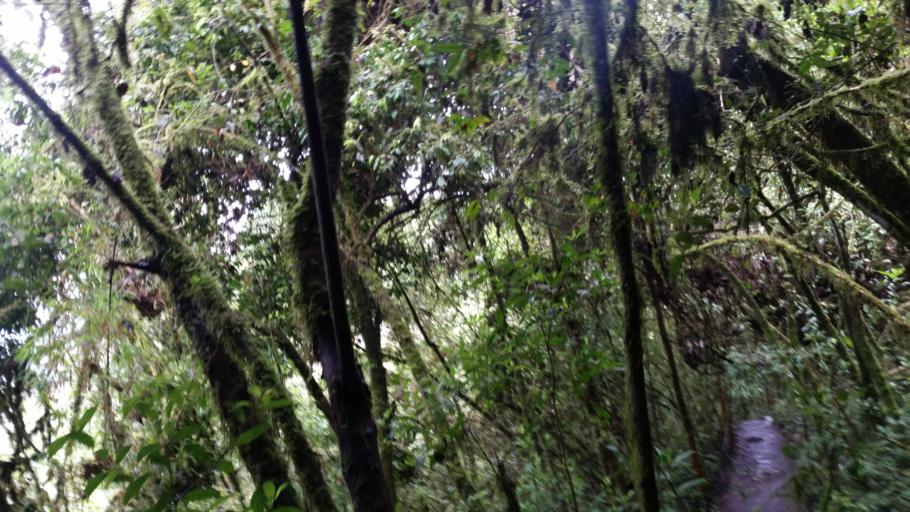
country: CO
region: Cundinamarca
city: Choachi
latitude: 4.5935
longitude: -73.9571
